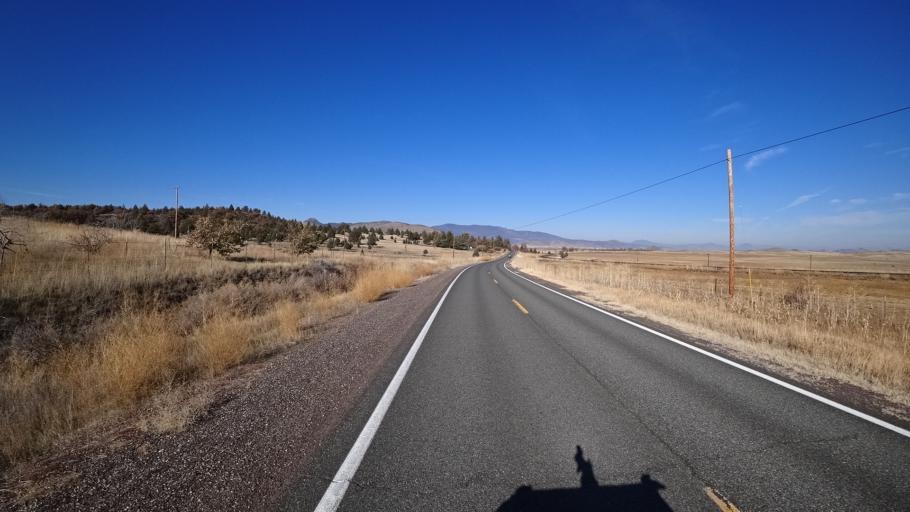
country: US
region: California
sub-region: Siskiyou County
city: Weed
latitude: 41.4917
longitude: -122.5078
